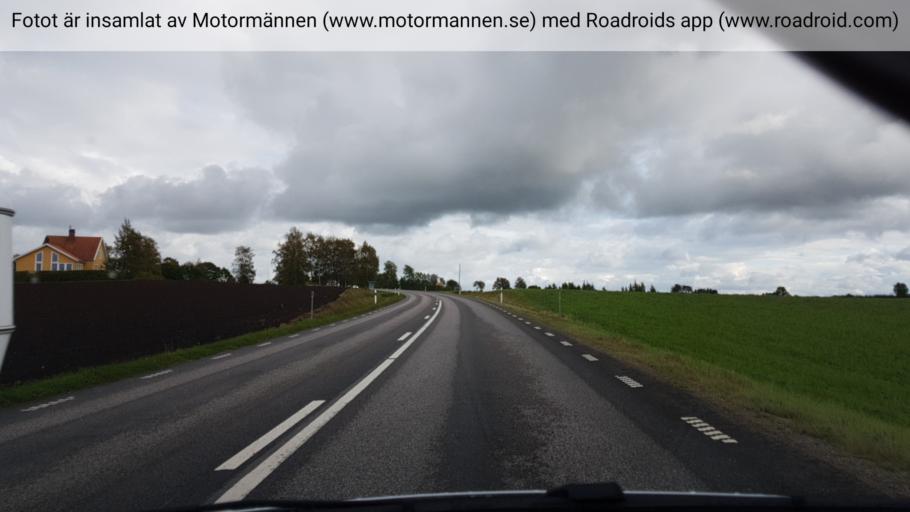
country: SE
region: Vaestra Goetaland
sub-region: Falkopings Kommun
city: Akarp
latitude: 58.0902
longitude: 13.7369
